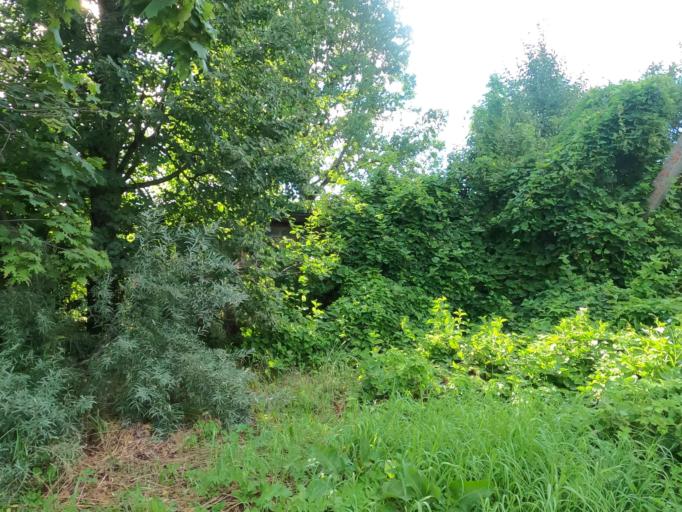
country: RU
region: Moskovskaya
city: Konobeyevo
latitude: 55.4073
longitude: 38.7170
